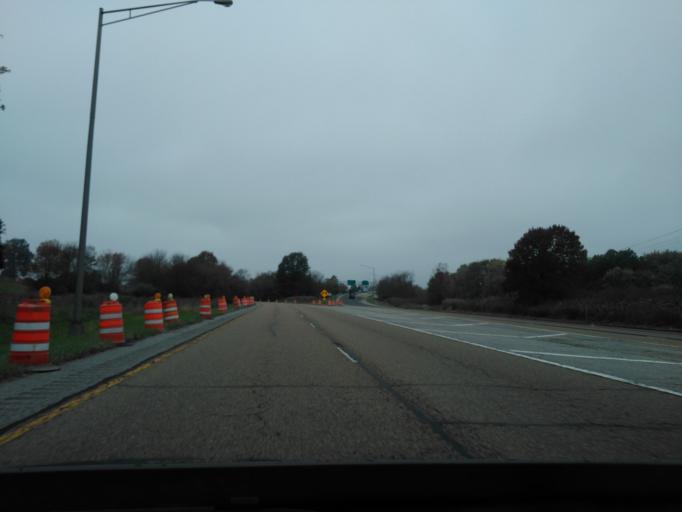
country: US
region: Illinois
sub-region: Madison County
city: Troy
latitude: 38.7527
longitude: -89.8979
